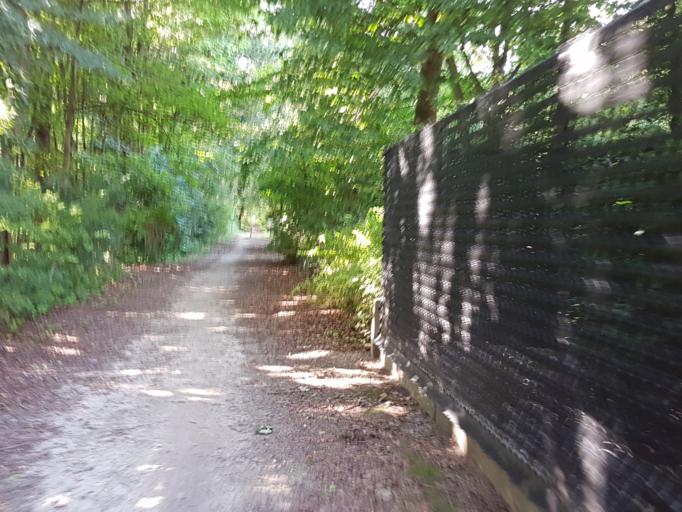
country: BE
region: Flanders
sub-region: Provincie Vlaams-Brabant
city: Machelen
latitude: 50.9178
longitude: 4.4718
